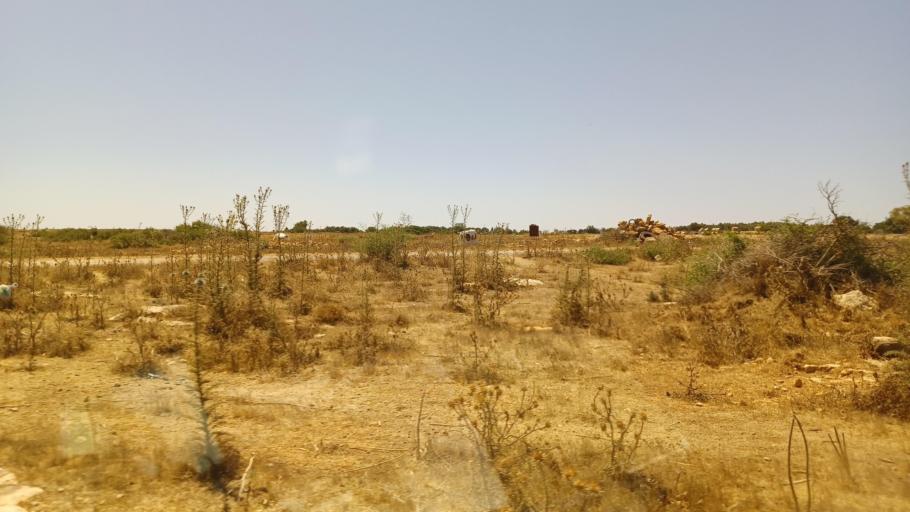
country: CY
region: Ammochostos
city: Avgorou
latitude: 35.0605
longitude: 33.8505
